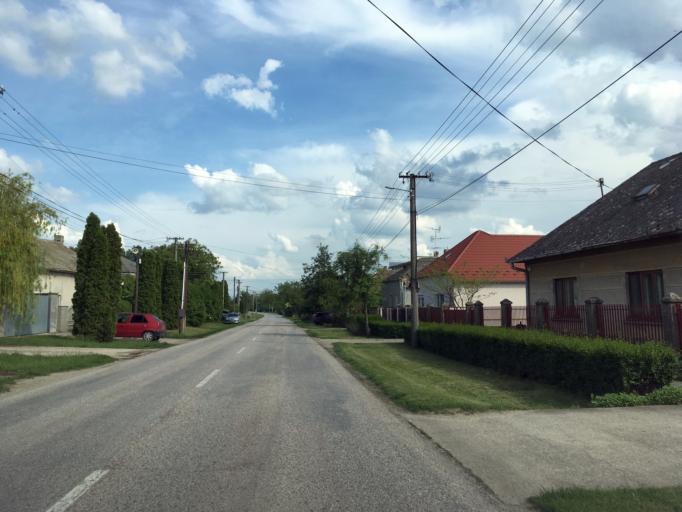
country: HU
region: Komarom-Esztergom
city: Almasfuzito
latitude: 47.8016
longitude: 18.2369
